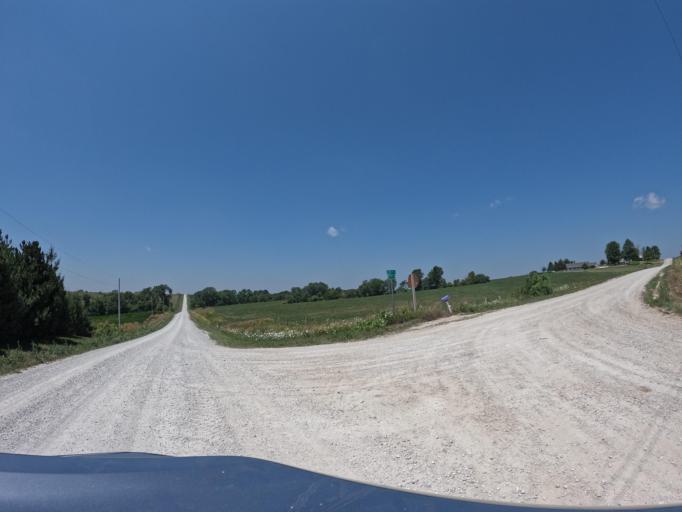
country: US
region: Iowa
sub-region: Keokuk County
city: Sigourney
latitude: 41.2579
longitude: -92.1696
